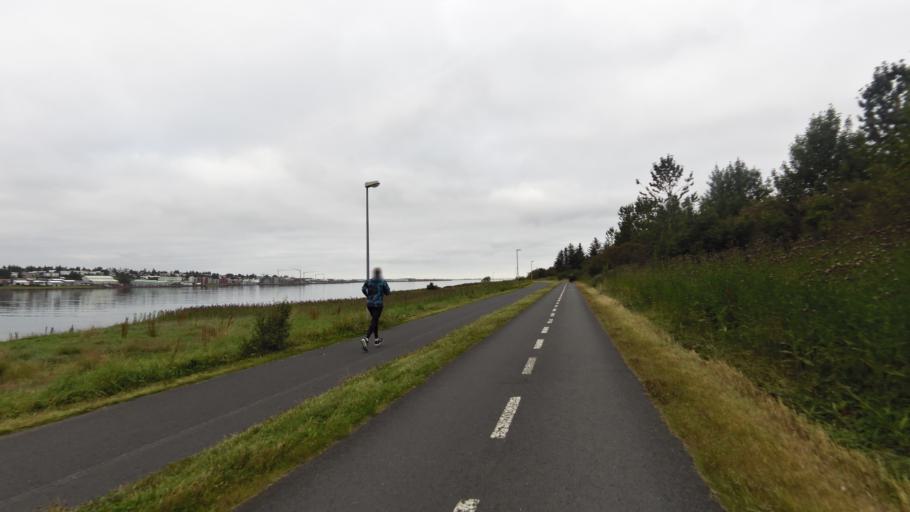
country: IS
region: Capital Region
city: Kopavogur
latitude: 64.1208
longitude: -21.9059
